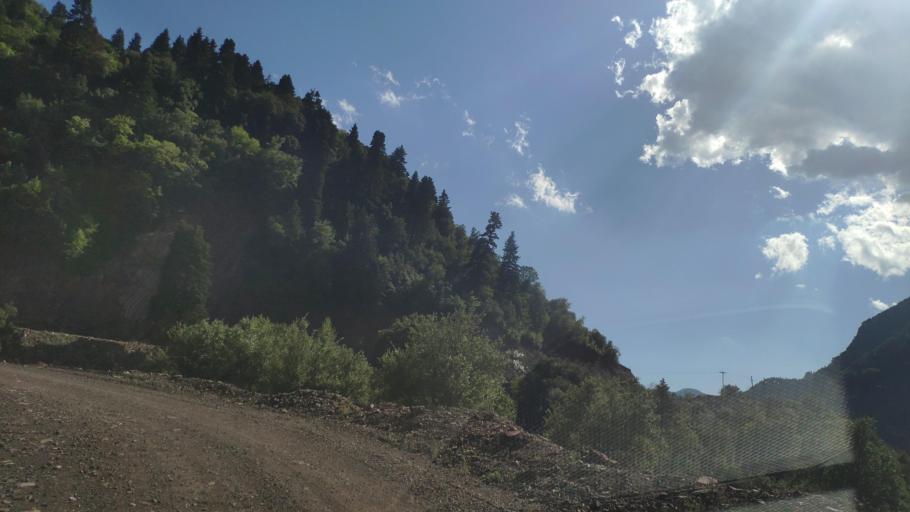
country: GR
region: Central Greece
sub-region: Nomos Evrytanias
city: Kerasochori
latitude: 39.1257
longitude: 21.6274
